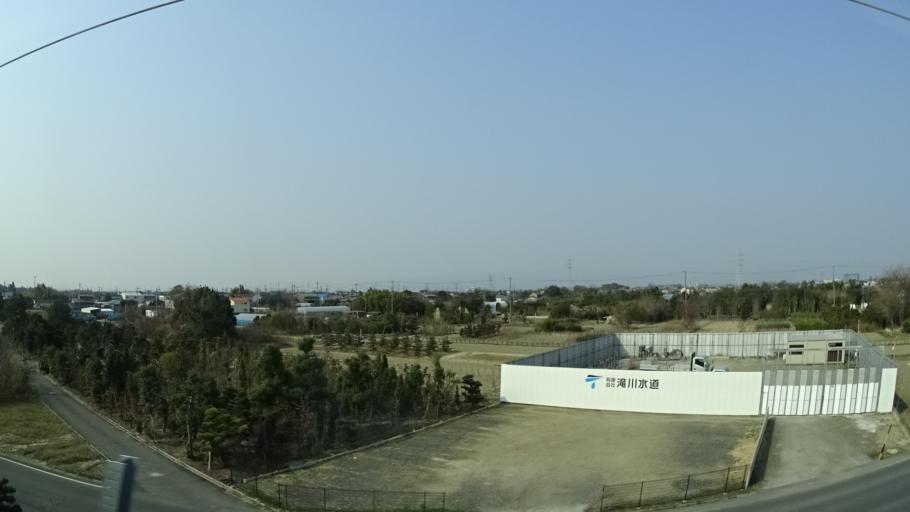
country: JP
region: Aichi
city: Inazawa
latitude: 35.2476
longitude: 136.7704
